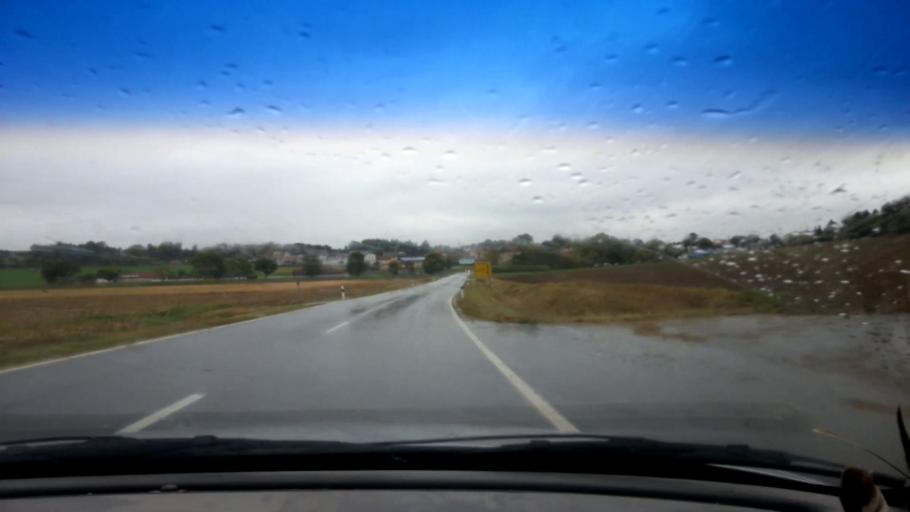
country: DE
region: Bavaria
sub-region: Upper Franconia
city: Konigsfeld
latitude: 49.9409
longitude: 11.1572
